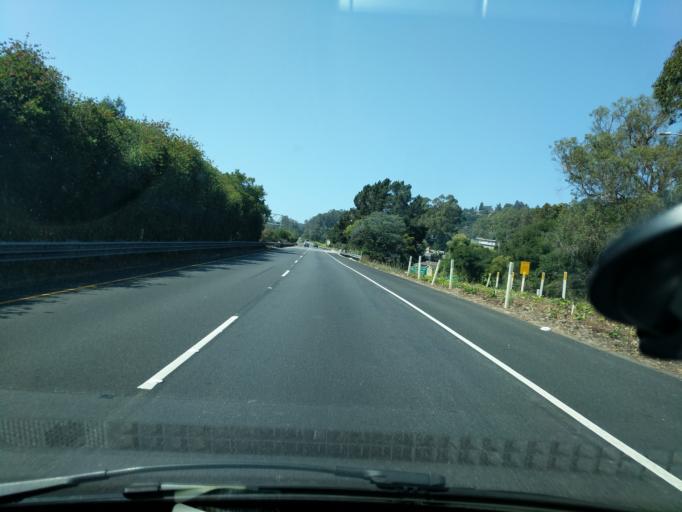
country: US
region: California
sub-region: Alameda County
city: Piedmont
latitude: 37.7931
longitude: -122.1812
